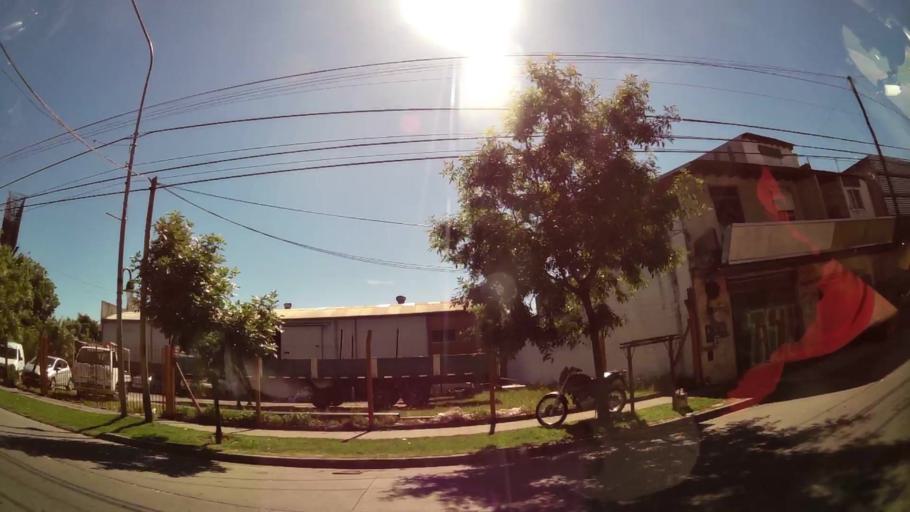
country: AR
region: Buenos Aires
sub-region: Partido de Tigre
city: Tigre
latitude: -34.4861
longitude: -58.6200
